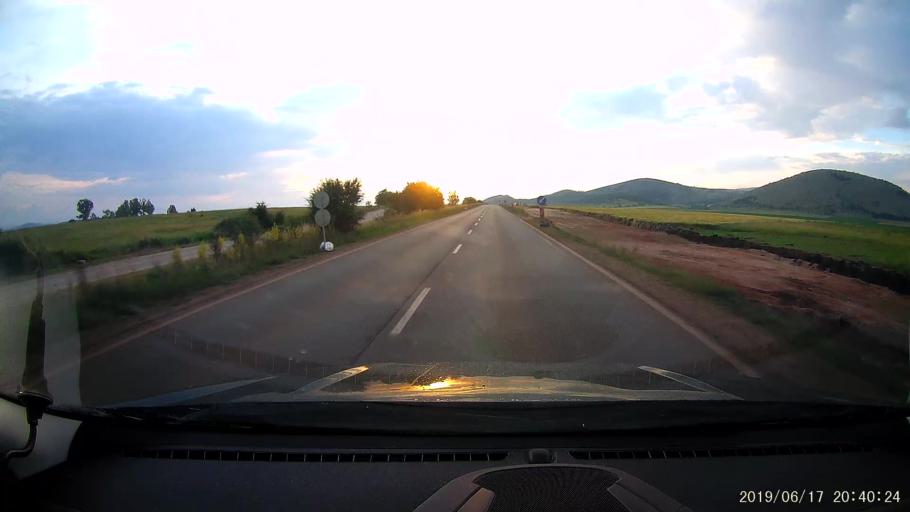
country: BG
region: Sofiya
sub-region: Obshtina Slivnitsa
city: Slivnitsa
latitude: 42.8864
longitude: 22.9872
